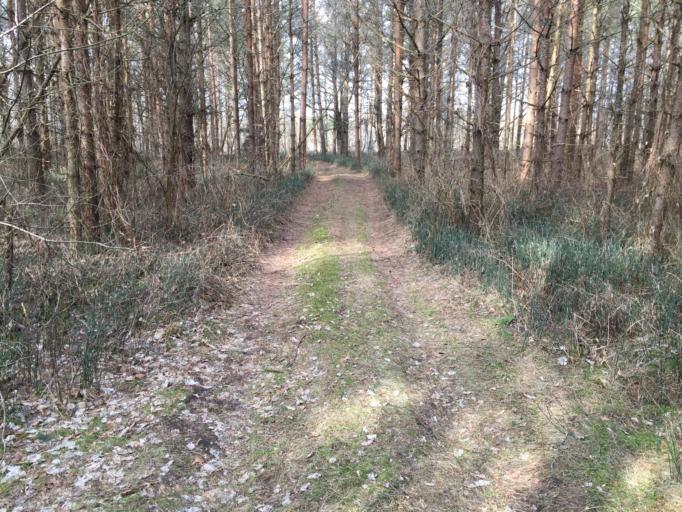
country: LV
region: Garkalne
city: Garkalne
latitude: 57.0796
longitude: 24.4366
